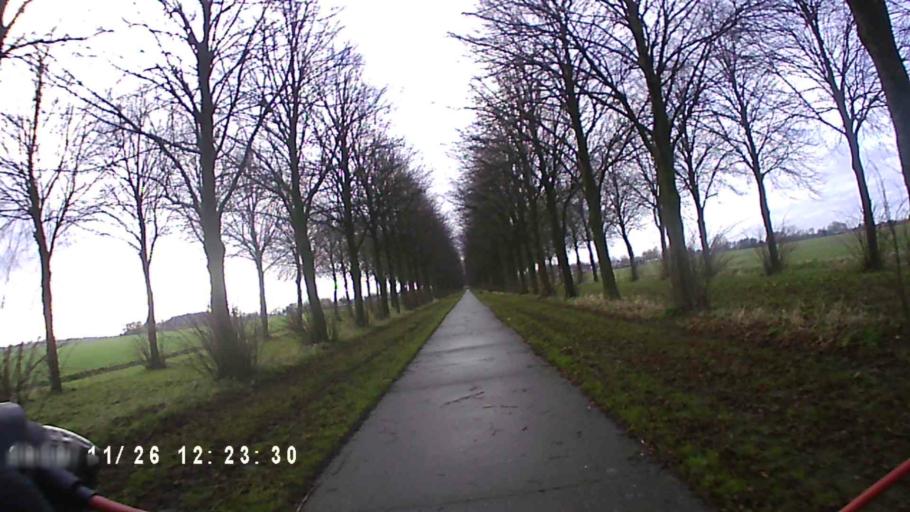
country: NL
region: Groningen
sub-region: Gemeente Bedum
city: Bedum
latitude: 53.3284
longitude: 6.7028
